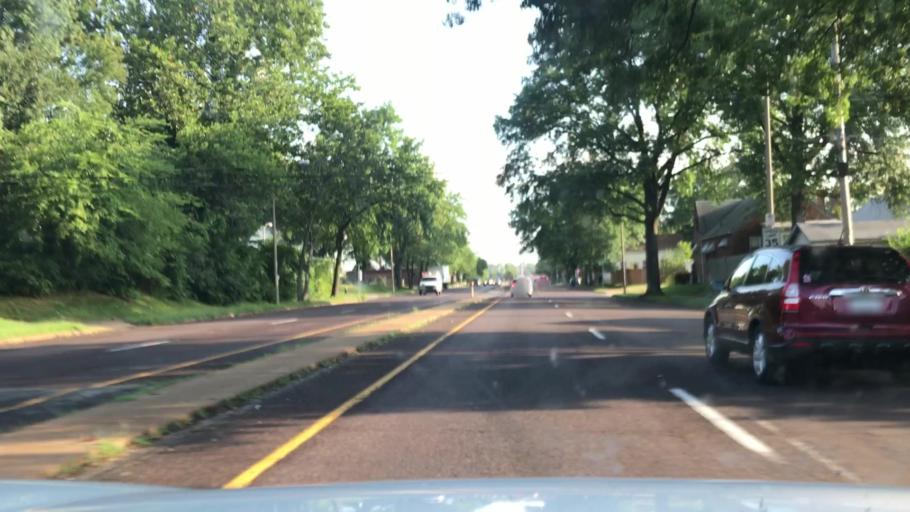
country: US
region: Missouri
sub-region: Saint Louis County
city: Maplewood
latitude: 38.6018
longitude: -90.3079
